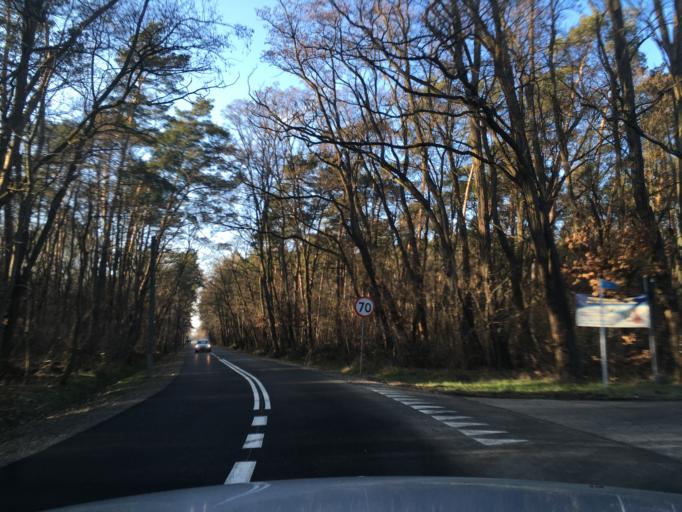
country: PL
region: Lodz Voivodeship
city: Zabia Wola
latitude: 52.0501
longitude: 20.7386
